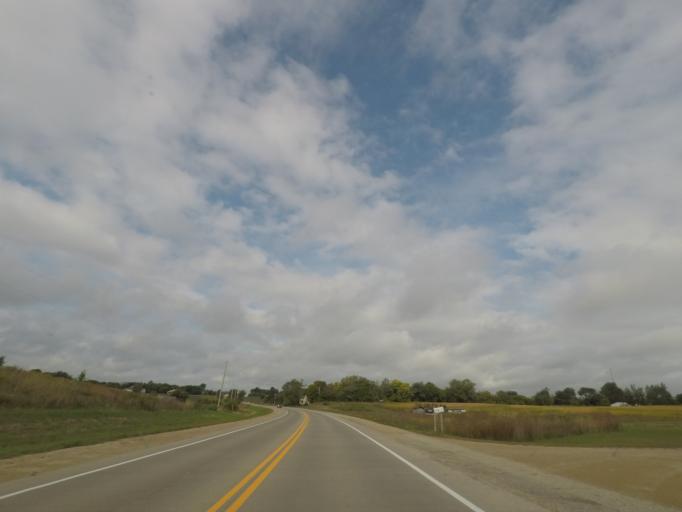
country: US
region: Wisconsin
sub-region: Dane County
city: Deerfield
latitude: 43.0366
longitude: -89.0947
